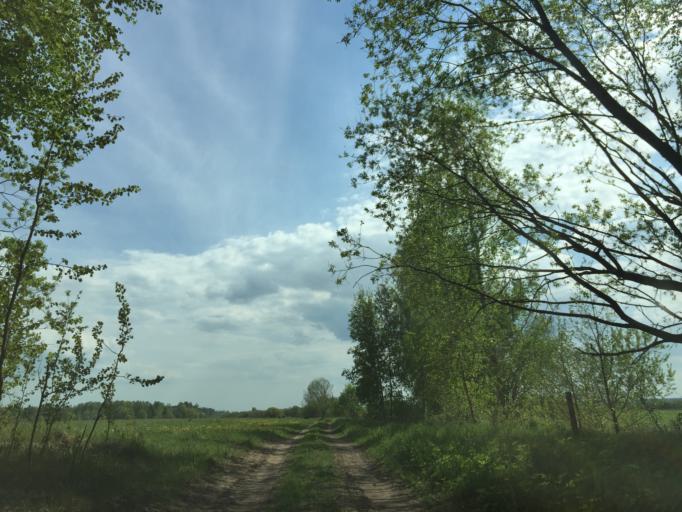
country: LV
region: Jelgava
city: Jelgava
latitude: 56.7301
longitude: 23.6763
